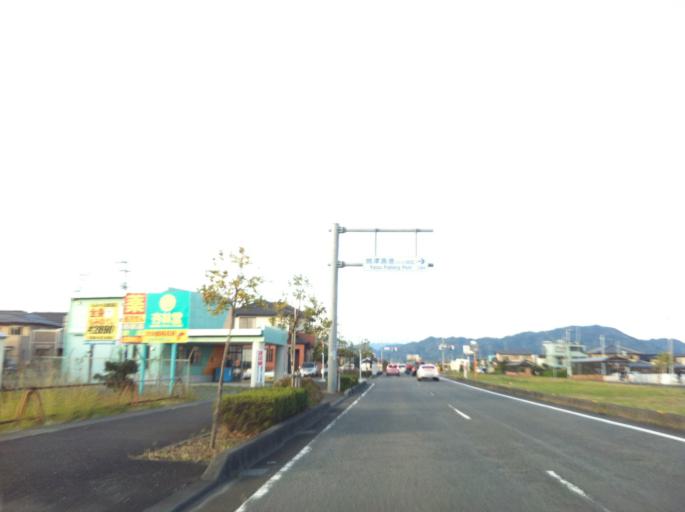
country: JP
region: Shizuoka
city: Yaizu
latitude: 34.8410
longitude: 138.3000
